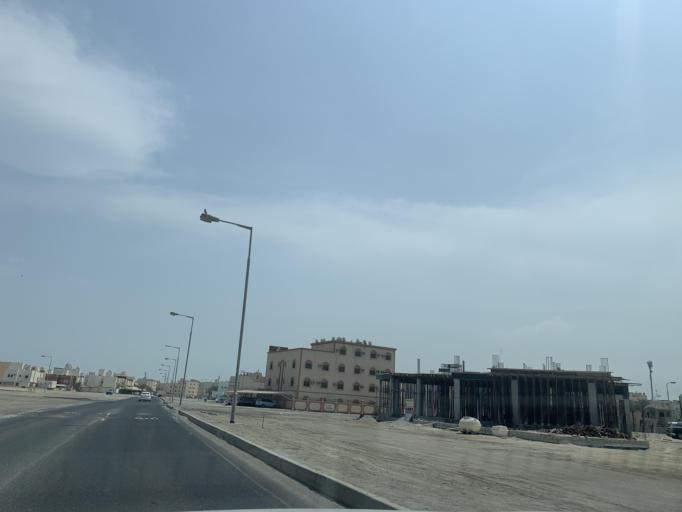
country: BH
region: Muharraq
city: Al Hadd
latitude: 26.2720
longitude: 50.6570
